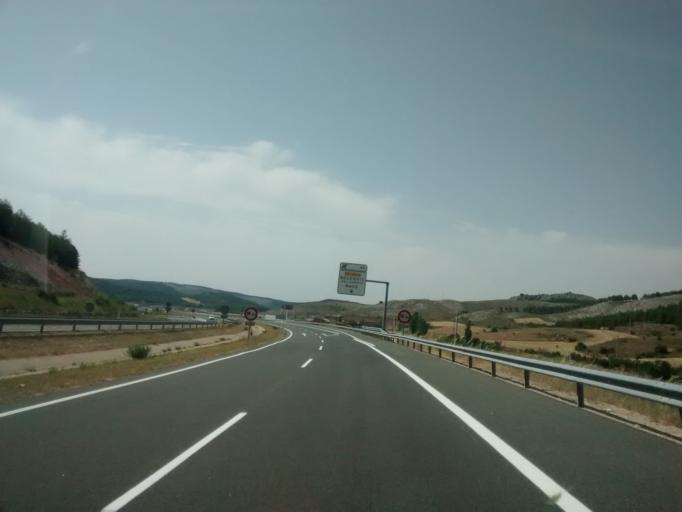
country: ES
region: Castille and Leon
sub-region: Provincia de Palencia
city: Alar del Rey
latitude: 42.7228
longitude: -4.2910
